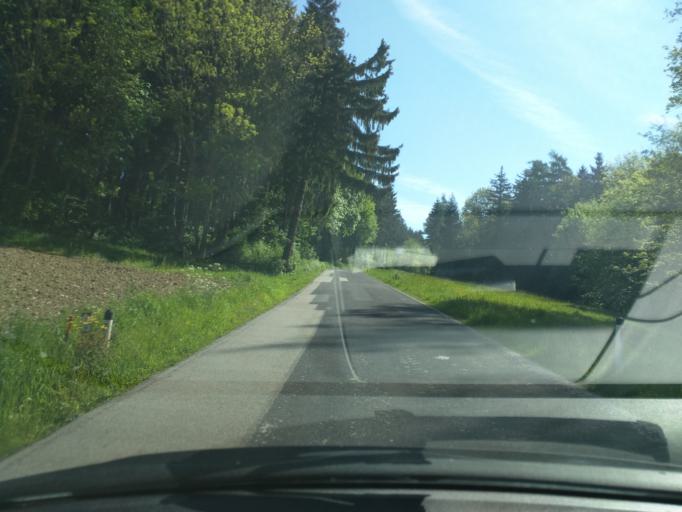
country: AT
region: Lower Austria
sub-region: Politischer Bezirk Amstetten
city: Euratsfeld
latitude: 48.0973
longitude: 14.9621
